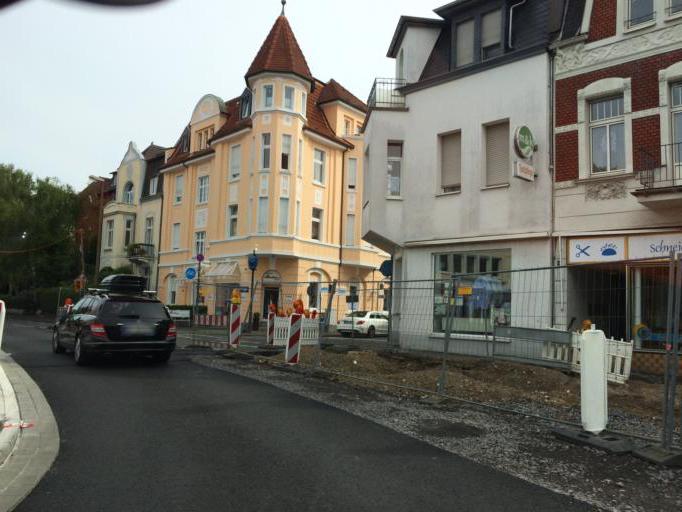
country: DE
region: North Rhine-Westphalia
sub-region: Regierungsbezirk Koln
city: Konigswinter
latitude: 50.6845
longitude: 7.1692
